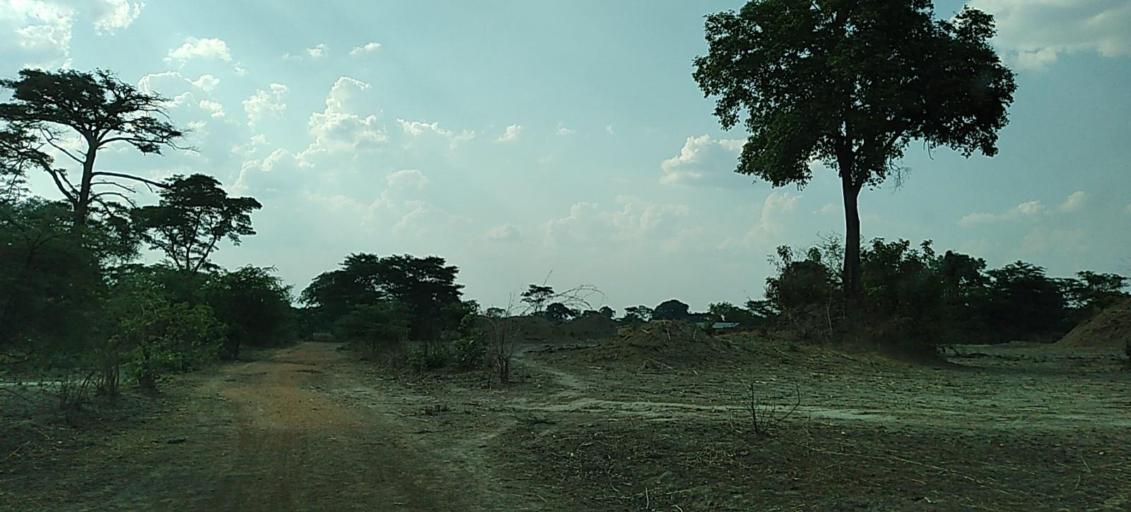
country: ZM
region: Copperbelt
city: Mpongwe
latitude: -13.4767
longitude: 28.0819
